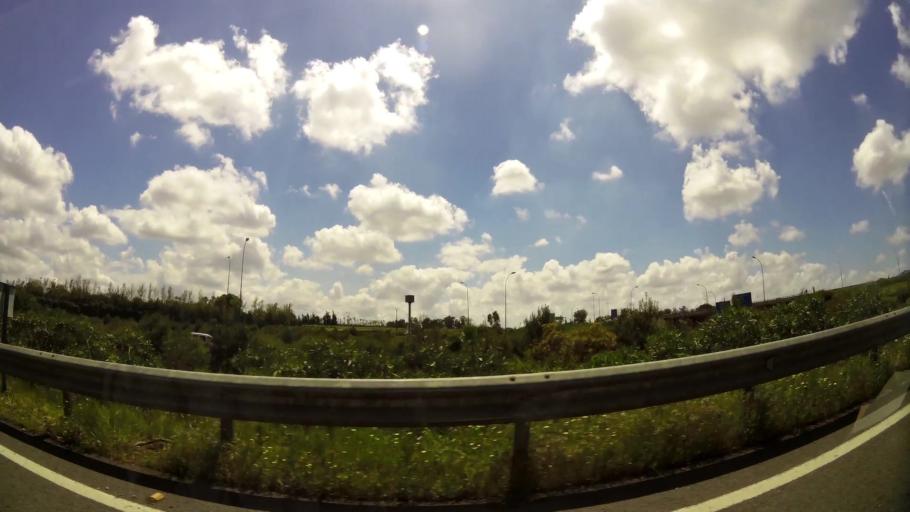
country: MA
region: Grand Casablanca
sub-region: Nouaceur
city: Bouskoura
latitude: 33.5013
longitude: -7.6267
